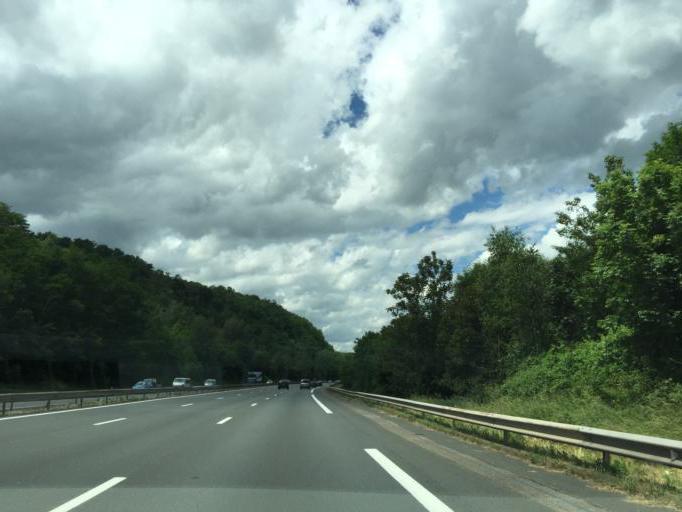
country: FR
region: Rhone-Alpes
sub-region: Departement de la Loire
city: La Fouillouse
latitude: 45.4960
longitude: 4.3155
